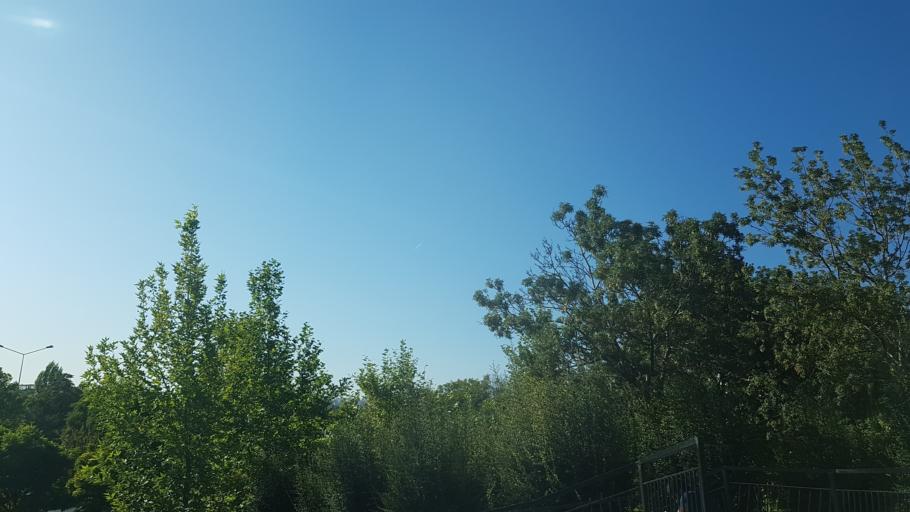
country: TR
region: Ankara
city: Ankara
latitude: 39.9537
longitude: 32.8567
